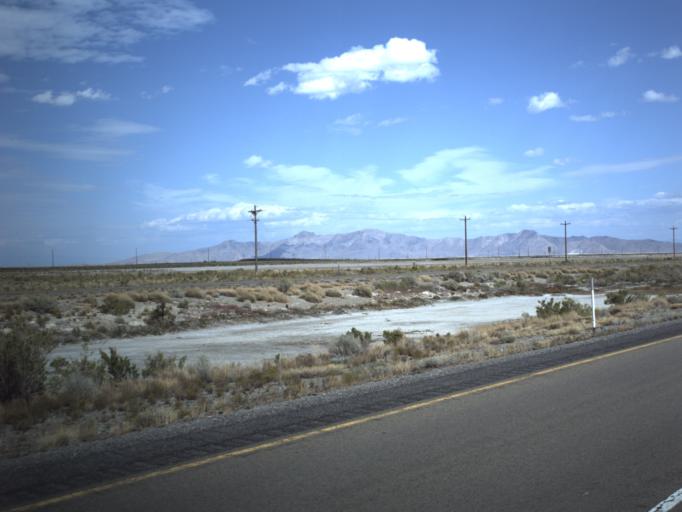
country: US
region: Utah
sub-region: Tooele County
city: Grantsville
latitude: 40.7536
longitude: -112.7331
